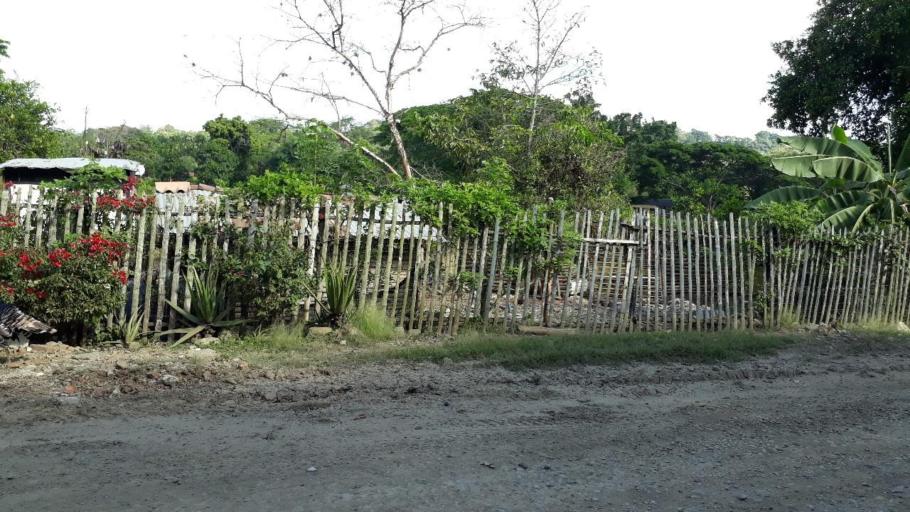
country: CO
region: Valle del Cauca
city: Jamundi
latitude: 3.1704
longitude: -76.5931
